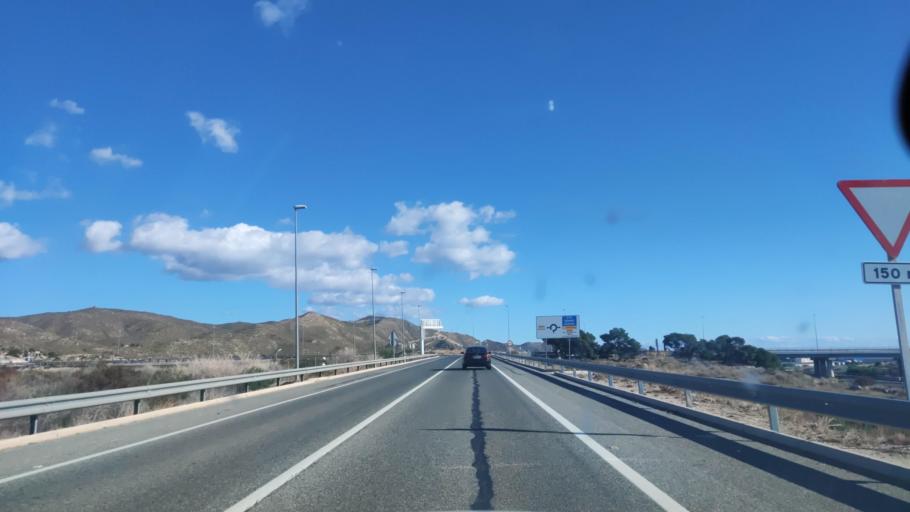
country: ES
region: Valencia
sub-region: Provincia de Alicante
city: el Campello
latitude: 38.4443
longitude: -0.3920
